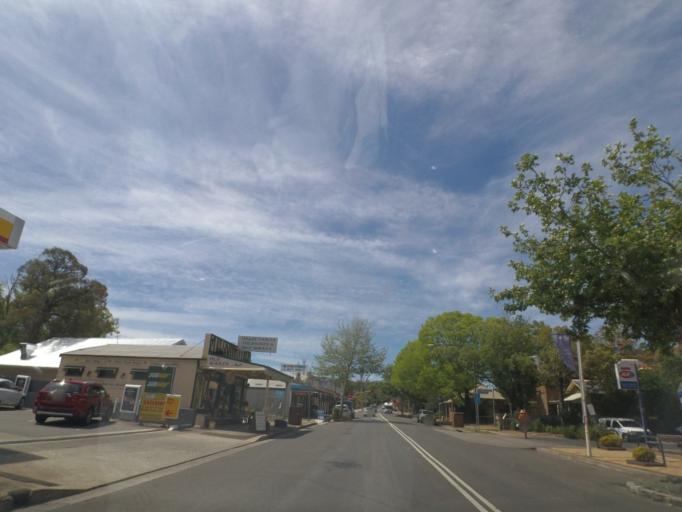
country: AU
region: New South Wales
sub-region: Wollondilly
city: Picton
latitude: -34.1686
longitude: 150.6118
